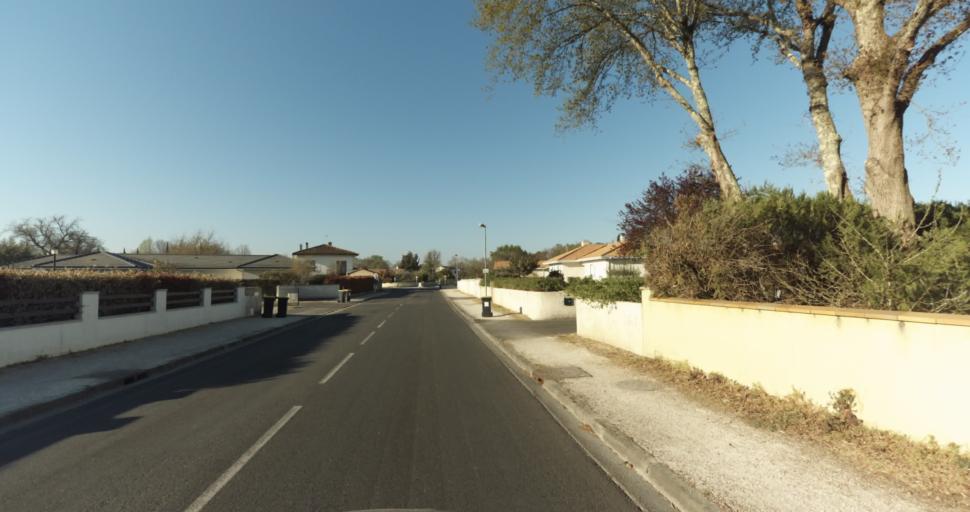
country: FR
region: Aquitaine
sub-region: Departement de la Gironde
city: Martignas-sur-Jalle
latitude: 44.8118
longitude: -0.7894
